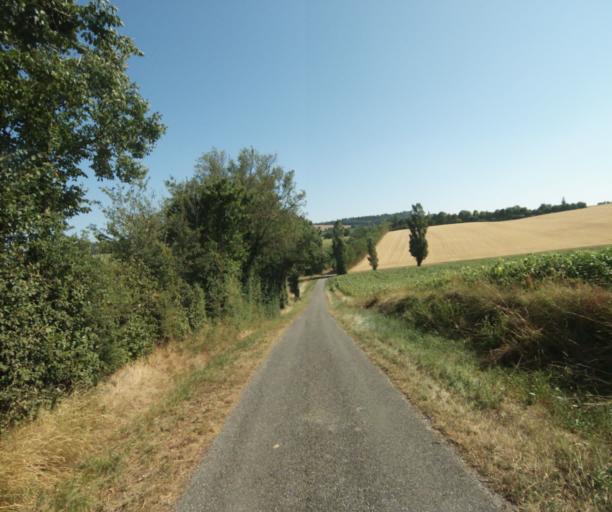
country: FR
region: Midi-Pyrenees
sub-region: Departement de la Haute-Garonne
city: Saint-Felix-Lauragais
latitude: 43.5042
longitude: 1.9195
